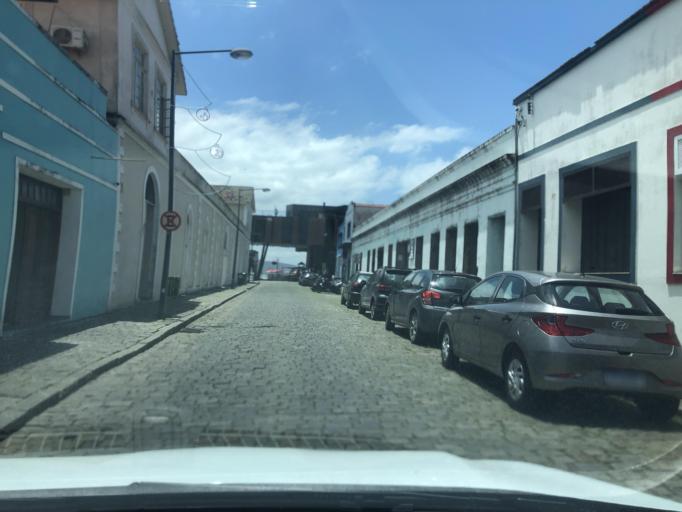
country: BR
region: Santa Catarina
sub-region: Sao Francisco Do Sul
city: Sao Francisco do Sul
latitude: -26.2418
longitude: -48.6401
